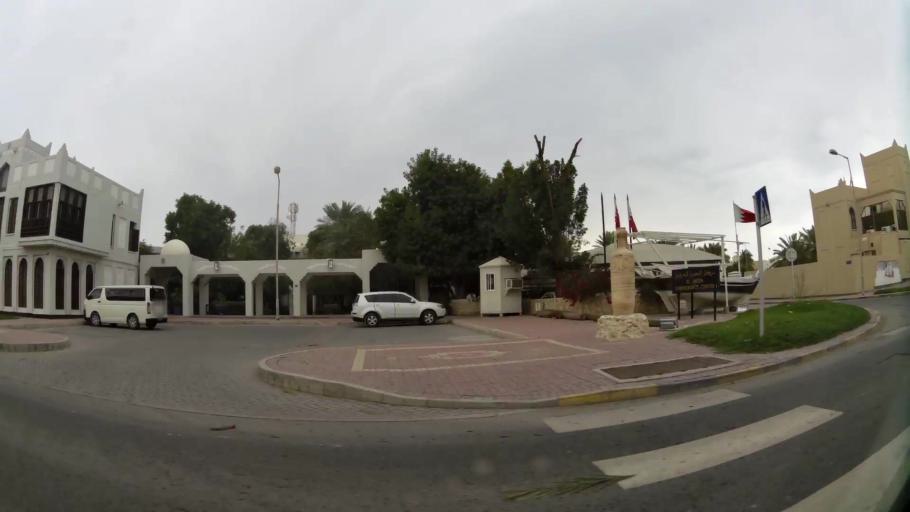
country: BH
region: Central Governorate
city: Madinat Hamad
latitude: 26.1639
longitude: 50.4511
